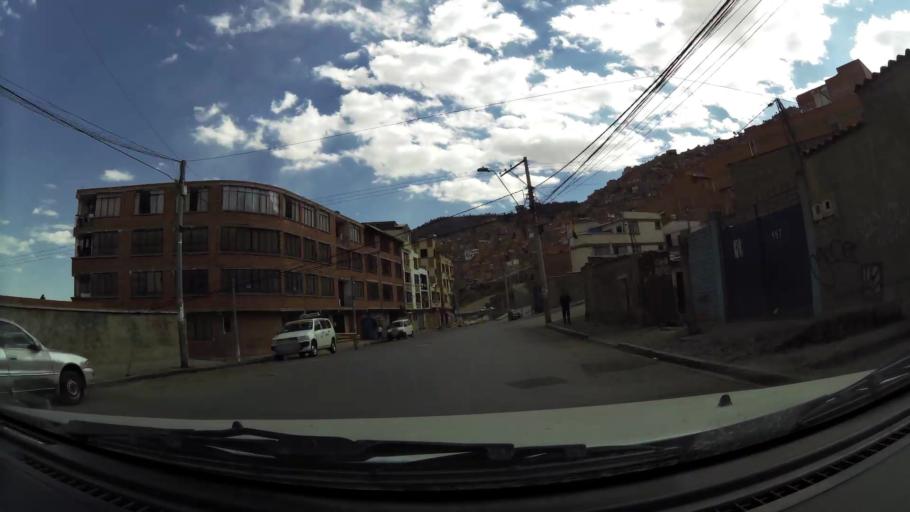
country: BO
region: La Paz
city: La Paz
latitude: -16.4739
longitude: -68.1199
